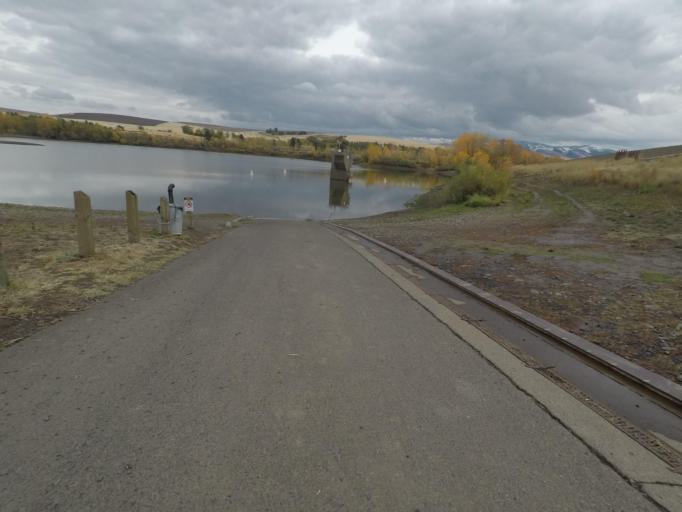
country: US
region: Washington
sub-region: Walla Walla County
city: Walla Walla East
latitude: 46.0653
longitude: -118.2641
